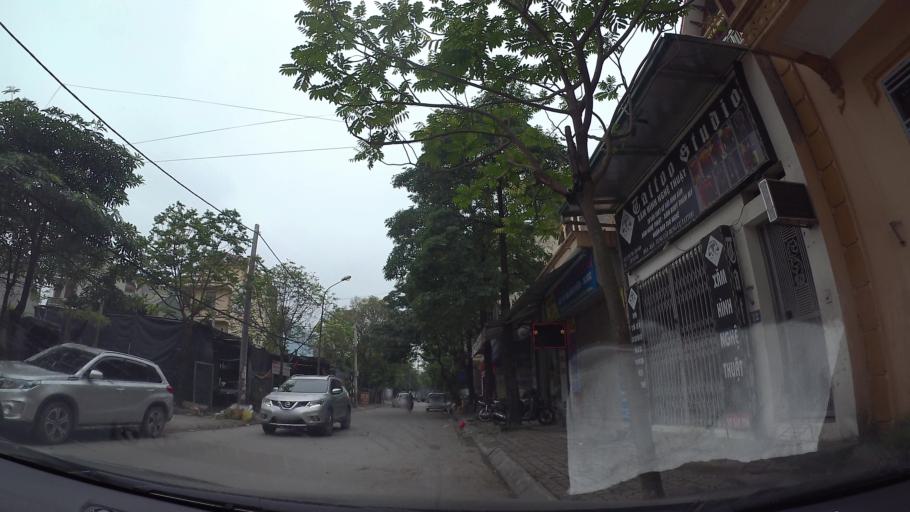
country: VN
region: Ha Noi
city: Hai BaTrung
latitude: 20.9795
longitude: 105.8842
